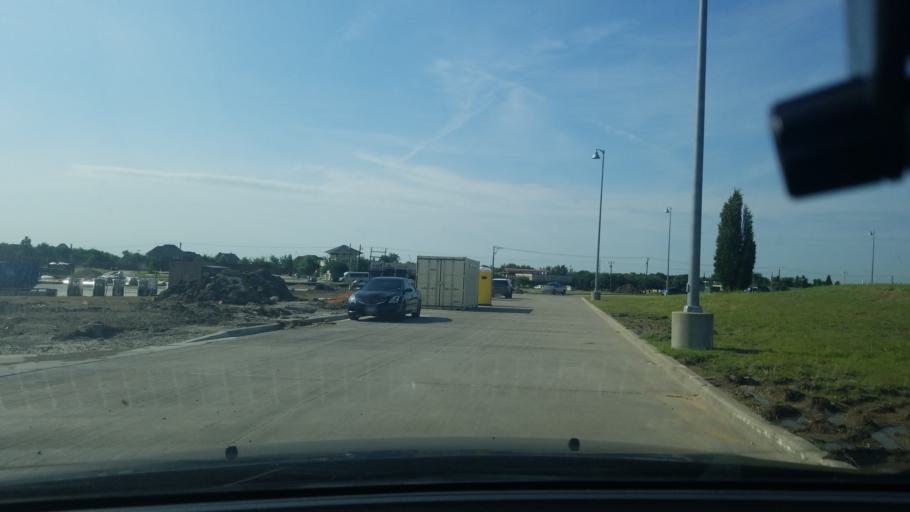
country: US
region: Texas
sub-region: Dallas County
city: Sunnyvale
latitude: 32.7836
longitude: -96.5652
